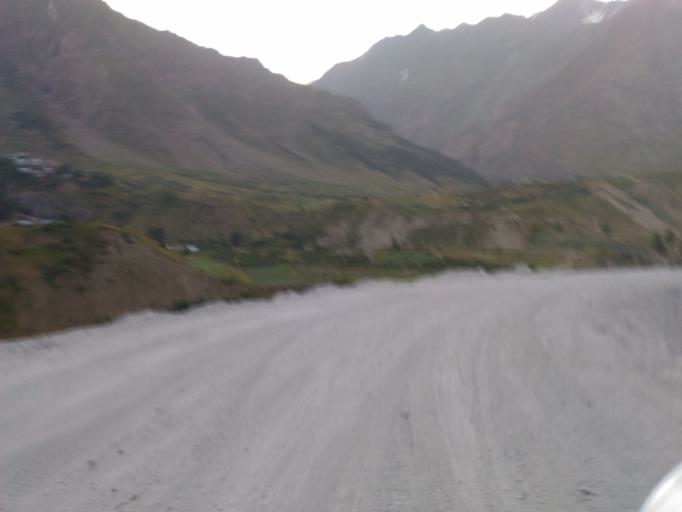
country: IN
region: Himachal Pradesh
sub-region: Lahul and Spiti
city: Kyelang
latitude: 32.5160
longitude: 76.9815
